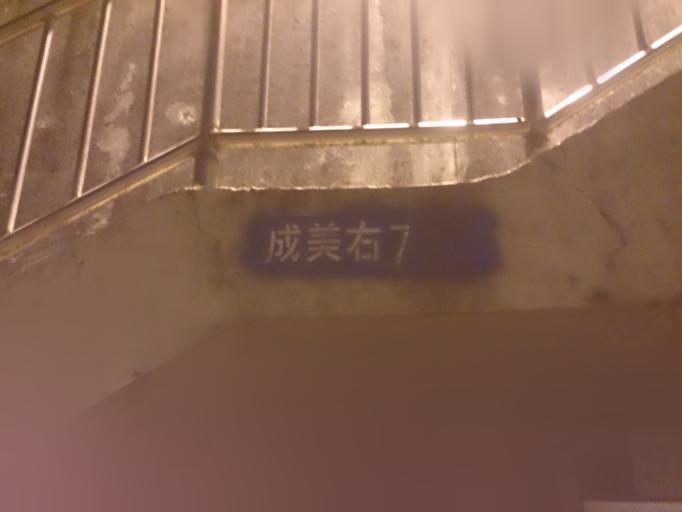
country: TW
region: Taipei
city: Taipei
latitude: 25.0536
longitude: 121.5807
